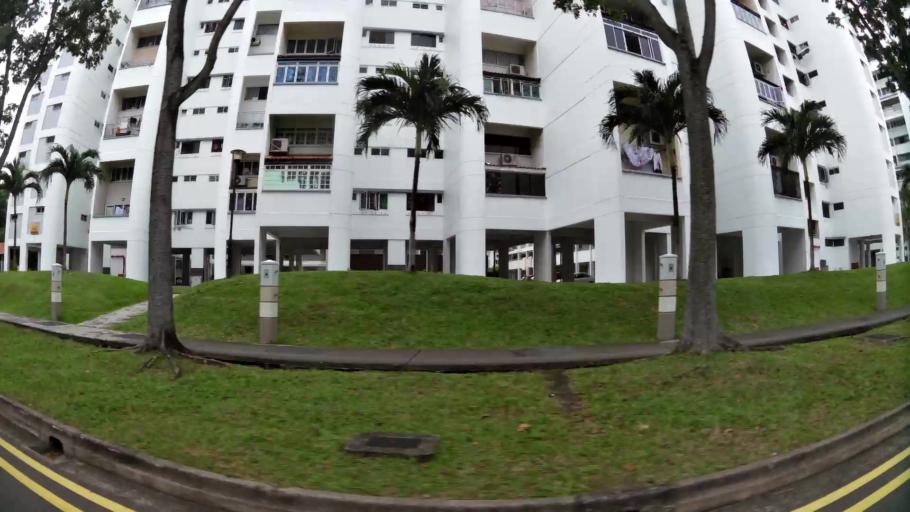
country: SG
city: Singapore
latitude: 1.3573
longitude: 103.8896
